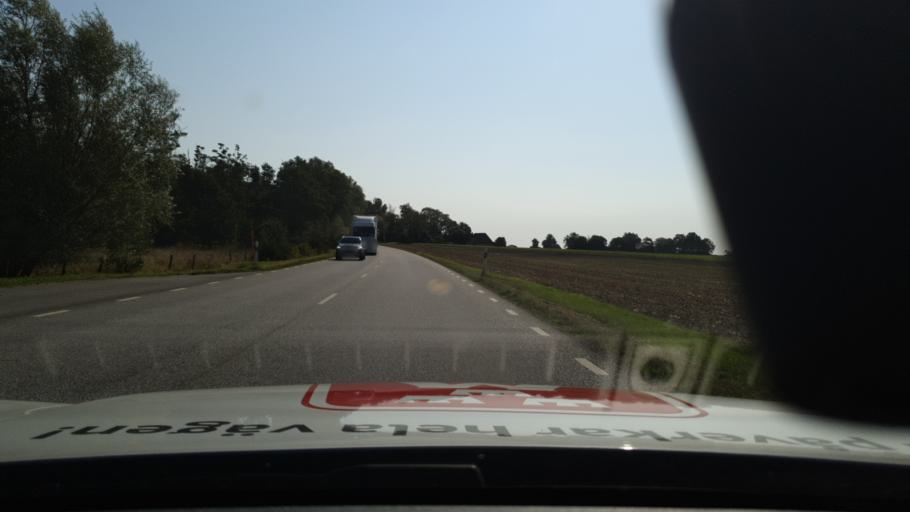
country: SE
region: Skane
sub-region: Kristianstads Kommun
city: Norra Asum
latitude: 55.9811
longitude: 14.1670
